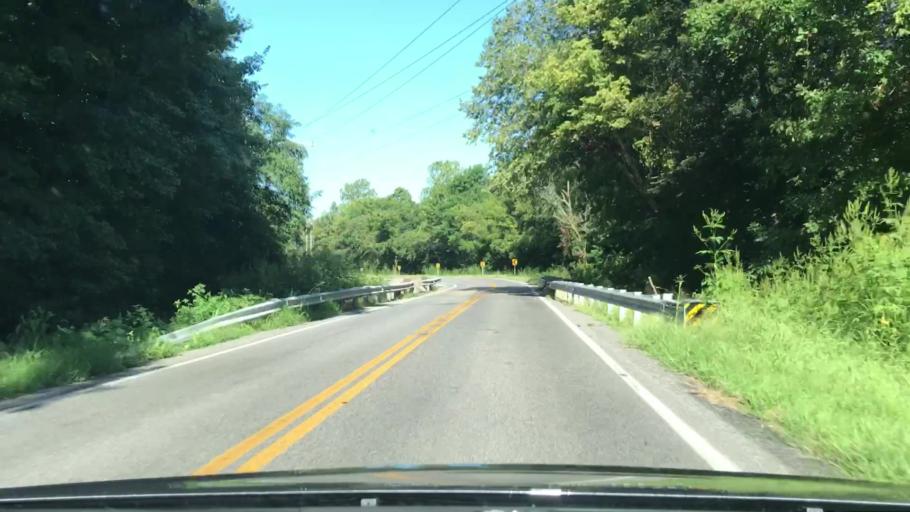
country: US
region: Kentucky
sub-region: Graves County
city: Mayfield
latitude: 36.7817
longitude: -88.5255
